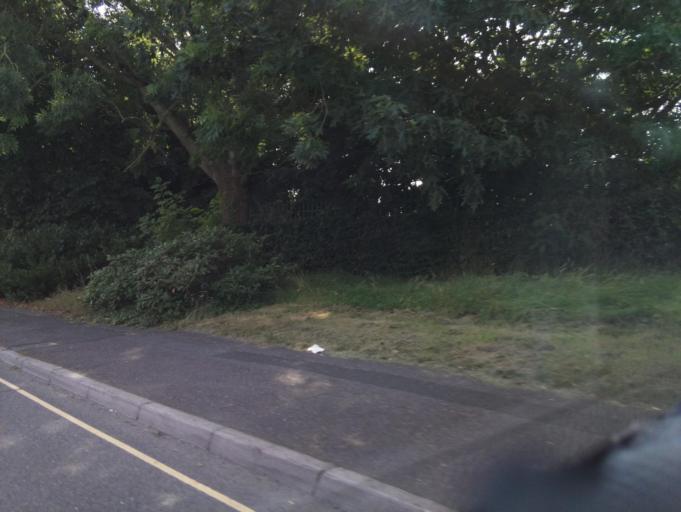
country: GB
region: England
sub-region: Devon
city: Exeter
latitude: 50.7059
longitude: -3.5380
